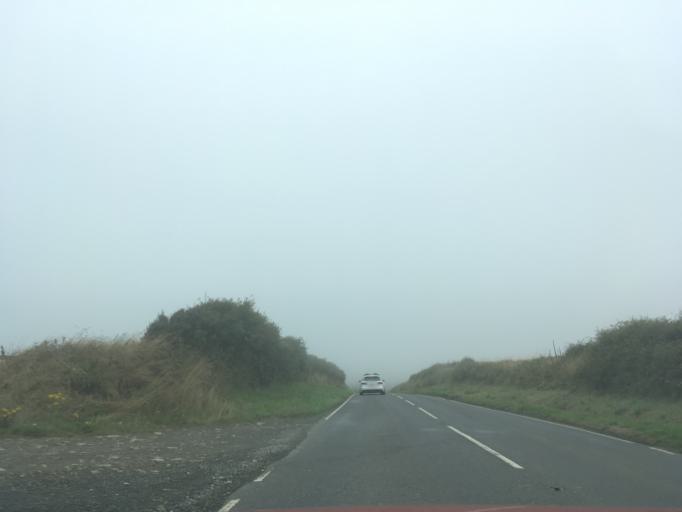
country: GB
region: Wales
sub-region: Pembrokeshire
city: Llanrhian
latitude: 51.8718
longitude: -5.1534
